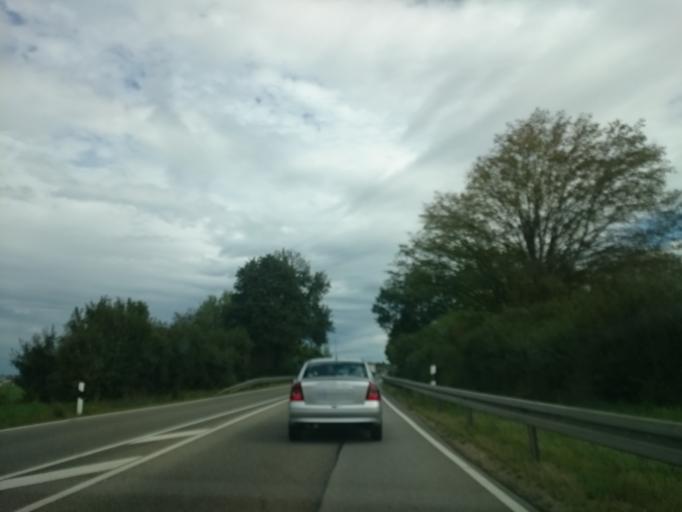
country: DE
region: Bavaria
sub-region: Swabia
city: Jengen
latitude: 47.9860
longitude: 10.6995
